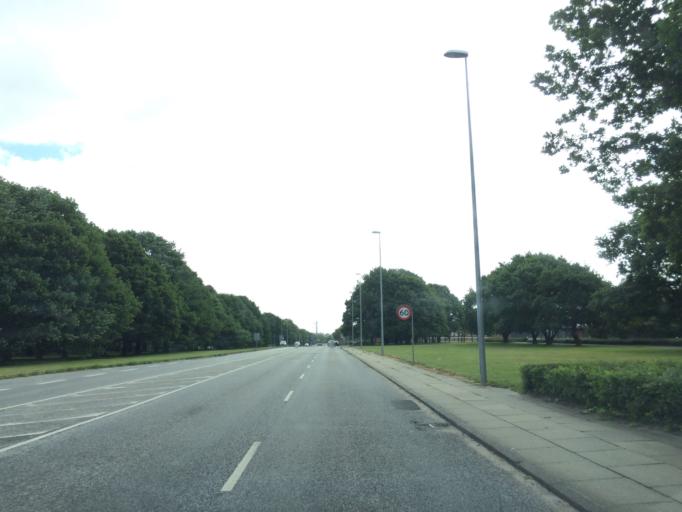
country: DK
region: Central Jutland
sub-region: Herning Kommune
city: Herning
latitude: 56.1454
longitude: 8.9631
